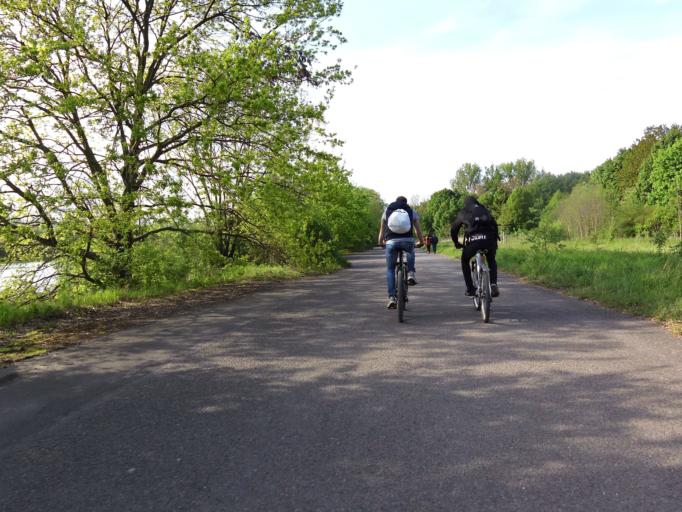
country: DE
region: Saxony
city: Leipzig
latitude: 51.3411
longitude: 12.3476
